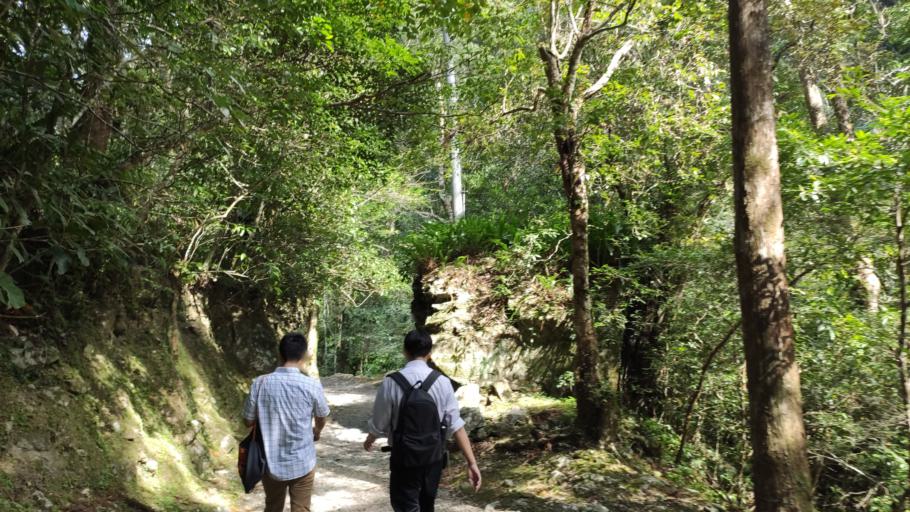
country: TW
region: Taiwan
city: Daxi
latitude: 24.8210
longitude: 121.4499
